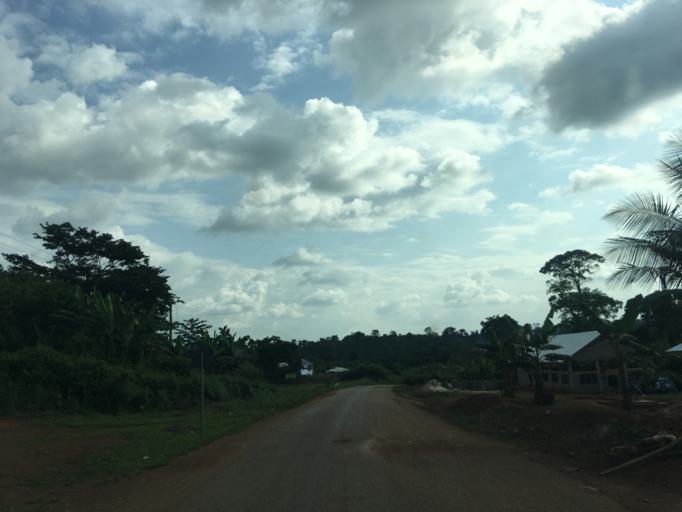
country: GH
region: Western
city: Bibiani
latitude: 6.7844
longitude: -2.5446
